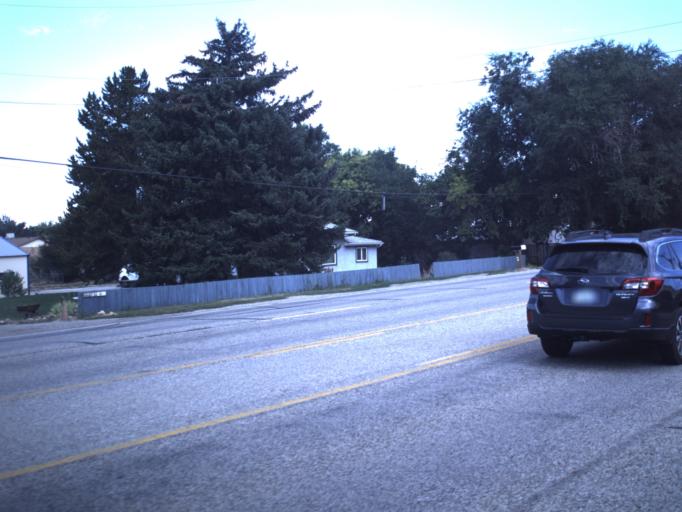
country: US
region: Utah
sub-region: Box Elder County
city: Willard
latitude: 41.4267
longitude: -112.0356
